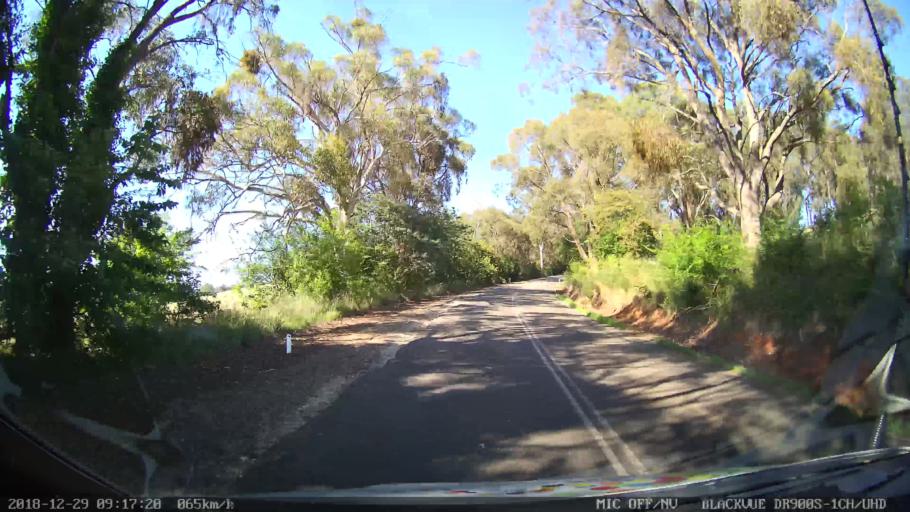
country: AU
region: New South Wales
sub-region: Upper Lachlan Shire
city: Crookwell
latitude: -34.4656
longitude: 149.4457
